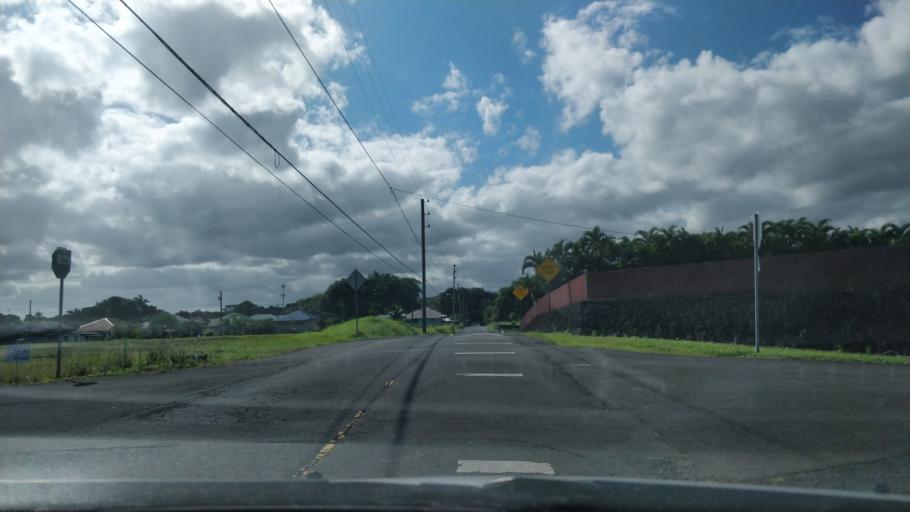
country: US
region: Hawaii
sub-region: Hawaii County
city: Hilo
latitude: 19.6686
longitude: -155.1055
